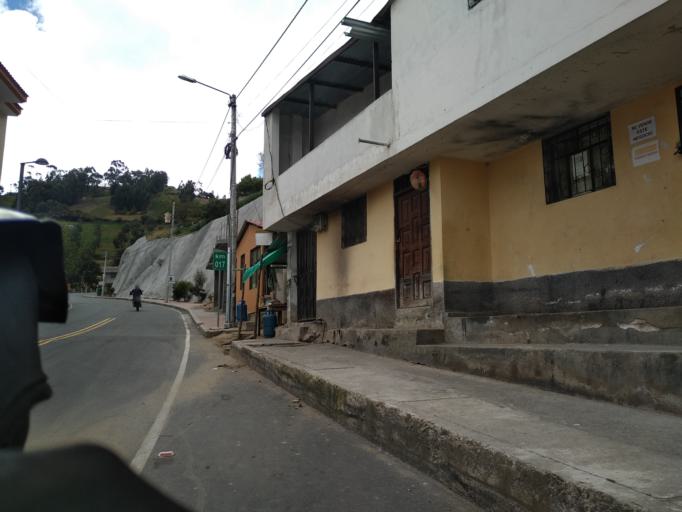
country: EC
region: Cotopaxi
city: Saquisili
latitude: -0.7995
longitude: -78.9209
